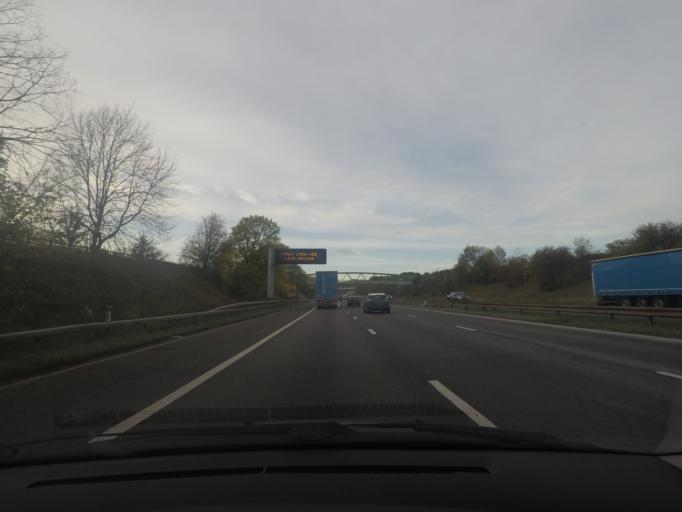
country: GB
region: England
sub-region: Barnsley
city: Stainborough
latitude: 53.5320
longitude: -1.4997
